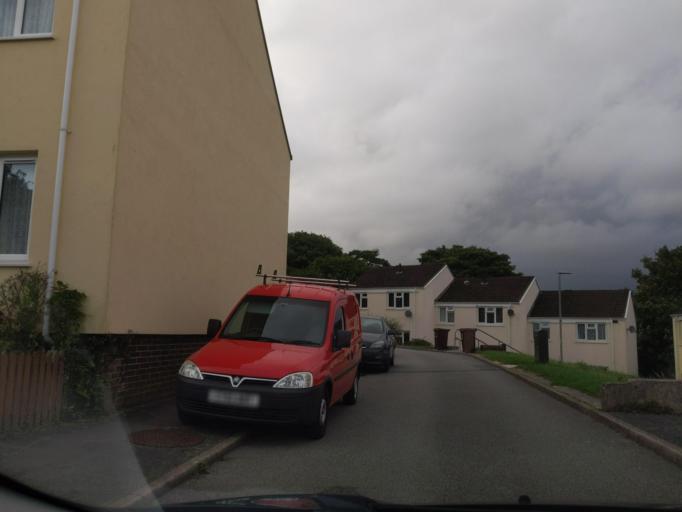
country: GB
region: England
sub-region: Devon
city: Plympton
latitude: 50.4056
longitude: -4.0918
